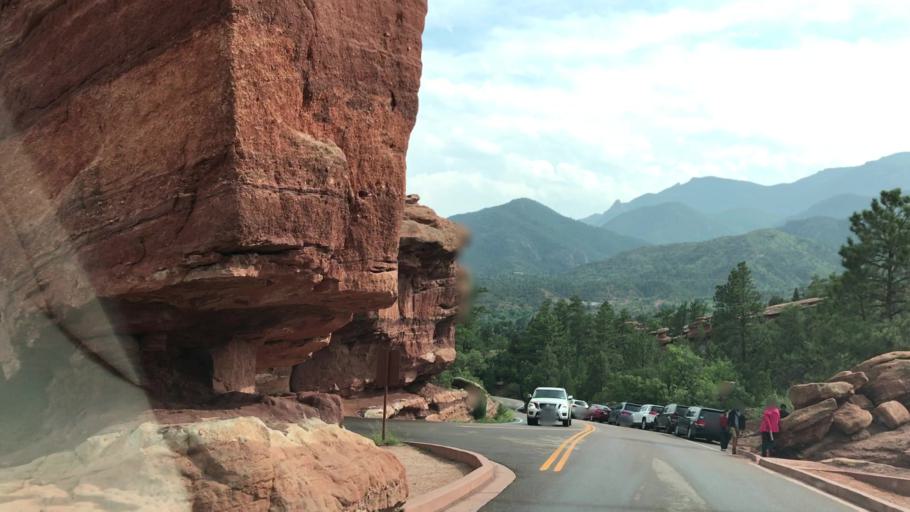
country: US
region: Colorado
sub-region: El Paso County
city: Manitou Springs
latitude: 38.8647
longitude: -104.8974
